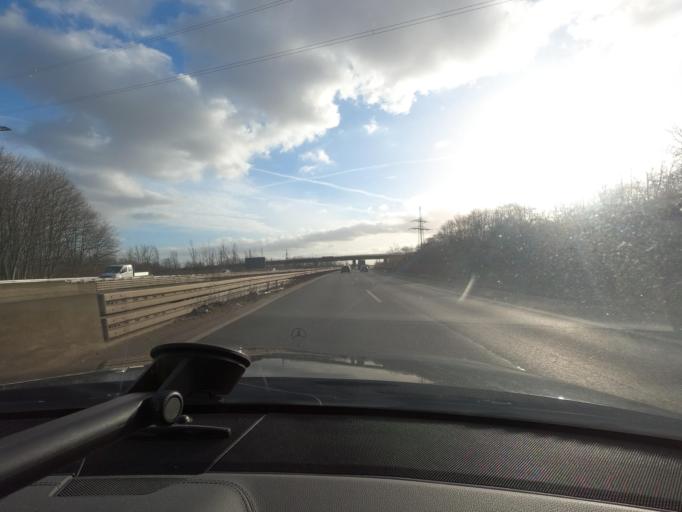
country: DE
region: North Rhine-Westphalia
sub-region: Regierungsbezirk Arnsberg
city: Dortmund
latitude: 51.5358
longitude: 7.5180
